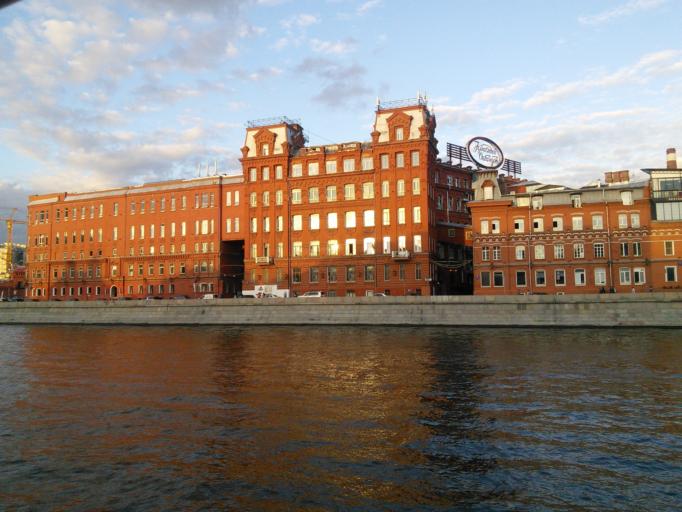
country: RU
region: Moscow
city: Moscow
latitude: 55.7405
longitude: 37.6072
